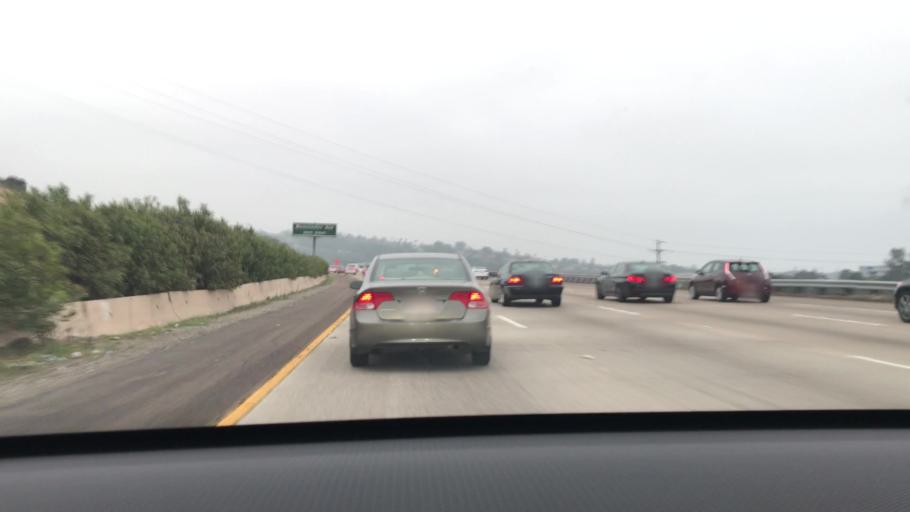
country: US
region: California
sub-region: San Diego County
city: Encinitas
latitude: 33.0191
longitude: -117.2730
